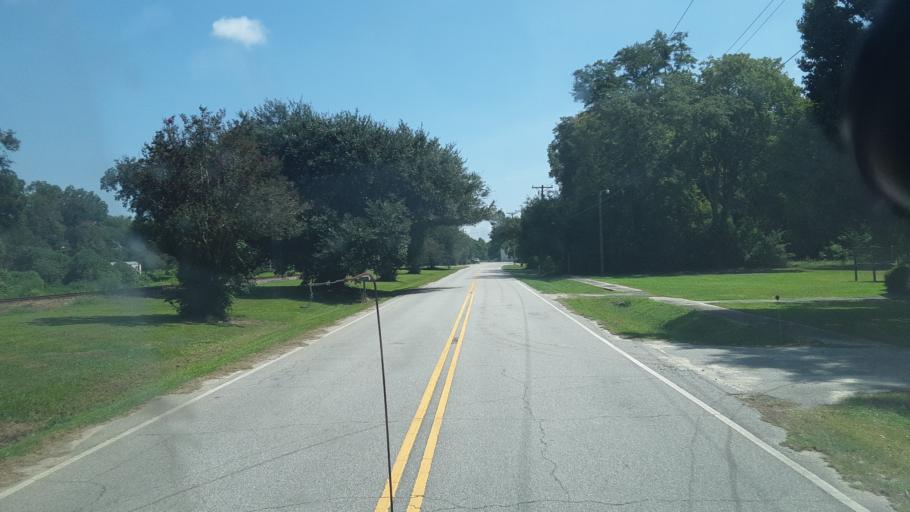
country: US
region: South Carolina
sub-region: Bamberg County
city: Bamberg
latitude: 33.3768
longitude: -81.0099
